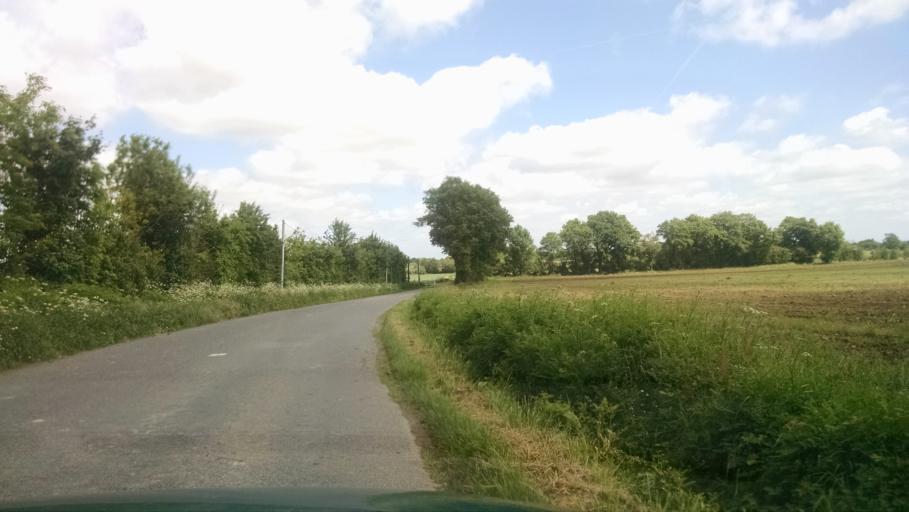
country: FR
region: Pays de la Loire
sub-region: Departement de la Loire-Atlantique
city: Saint-Hilaire-de-Clisson
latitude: 47.0744
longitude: -1.3106
